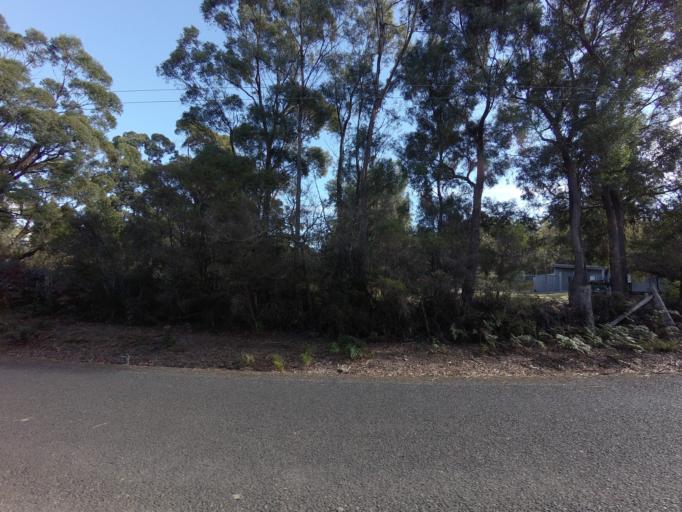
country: AU
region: Tasmania
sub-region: Clarence
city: Sandford
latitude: -42.9924
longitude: 147.7125
